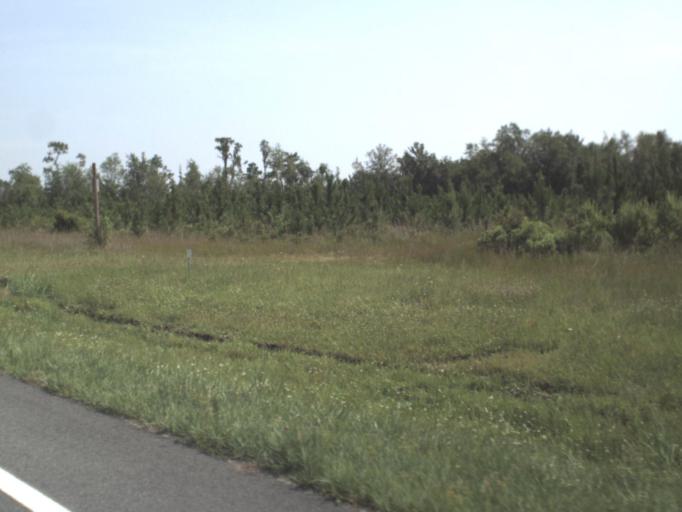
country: US
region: Georgia
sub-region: Echols County
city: Statenville
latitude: 30.6115
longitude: -83.0220
